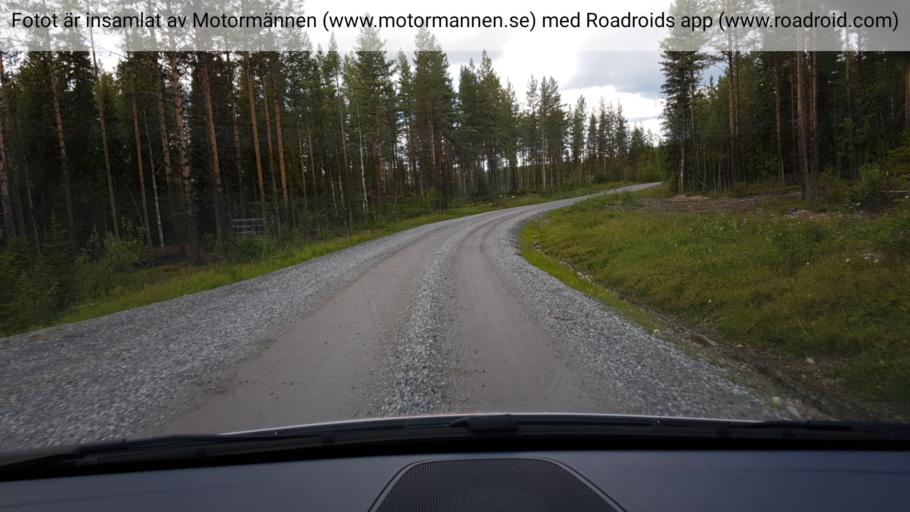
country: SE
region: Jaemtland
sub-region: Braecke Kommun
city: Braecke
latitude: 62.9635
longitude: 15.7323
